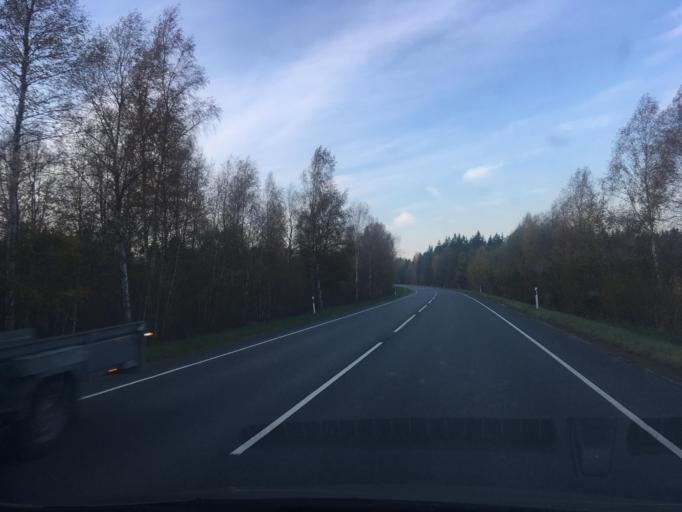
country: EE
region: Harju
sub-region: Nissi vald
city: Riisipere
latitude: 59.1174
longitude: 24.2718
